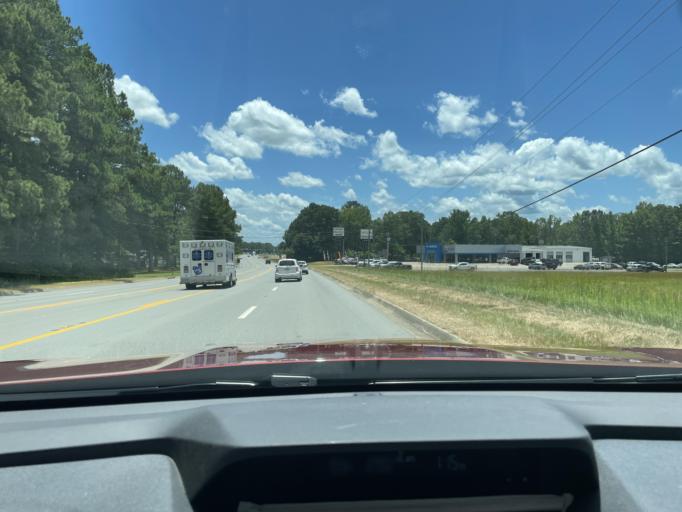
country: US
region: Arkansas
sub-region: Drew County
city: Monticello
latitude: 33.6524
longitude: -91.8025
